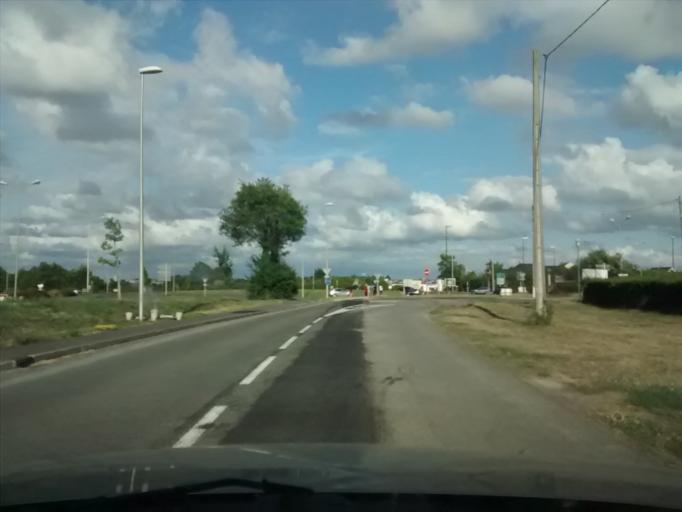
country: FR
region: Pays de la Loire
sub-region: Departement de la Mayenne
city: Change
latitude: 48.0807
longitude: -0.7975
